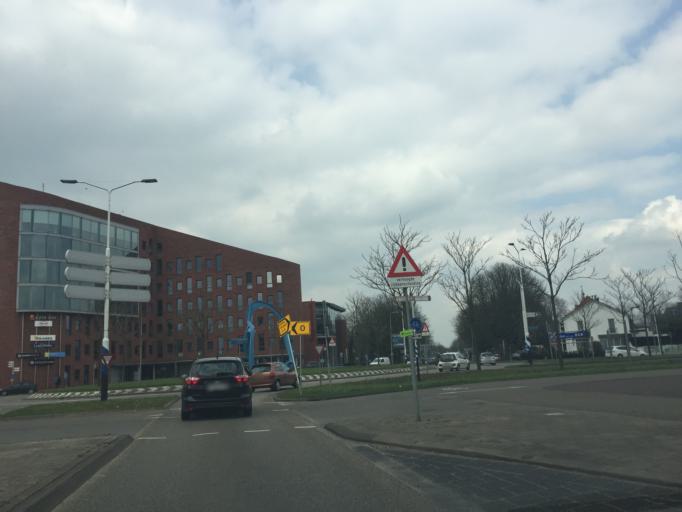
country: NL
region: South Holland
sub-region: Gemeente Alphen aan den Rijn
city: Alphen aan den Rijn
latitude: 52.1286
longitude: 4.6580
